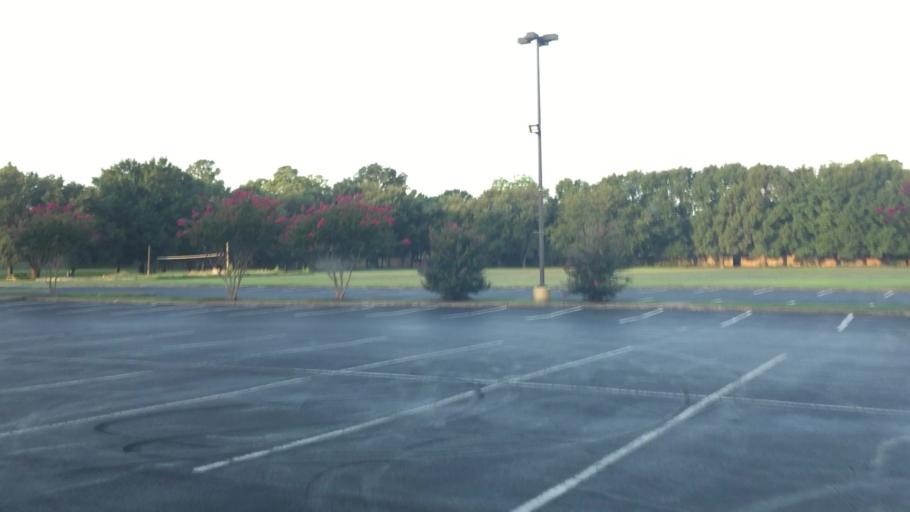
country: US
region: Texas
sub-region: Harris County
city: Hudson
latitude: 29.9915
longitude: -95.5025
